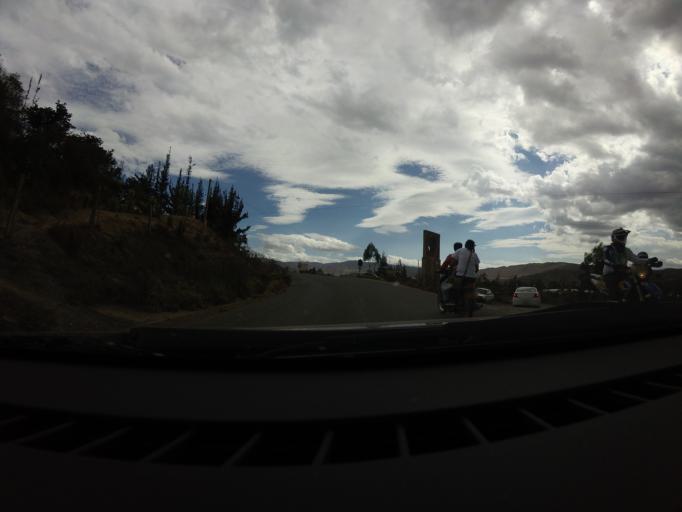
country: CO
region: Boyaca
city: Villa de Leiva
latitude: 5.6315
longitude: -73.5581
